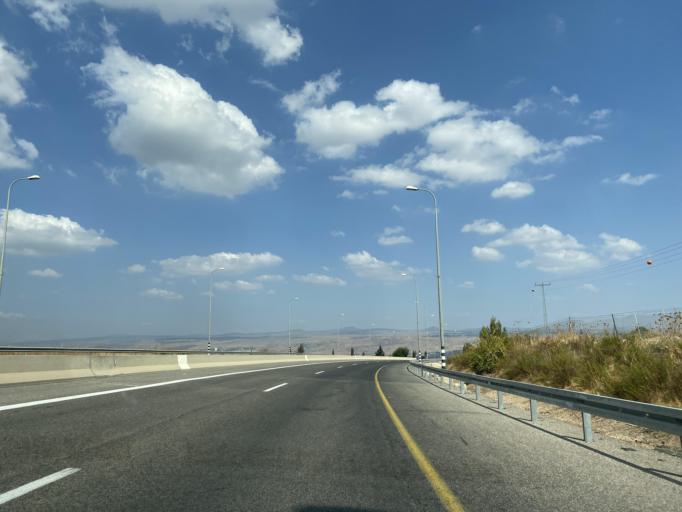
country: IL
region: Northern District
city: Rosh Pinna
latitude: 33.0274
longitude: 35.5593
